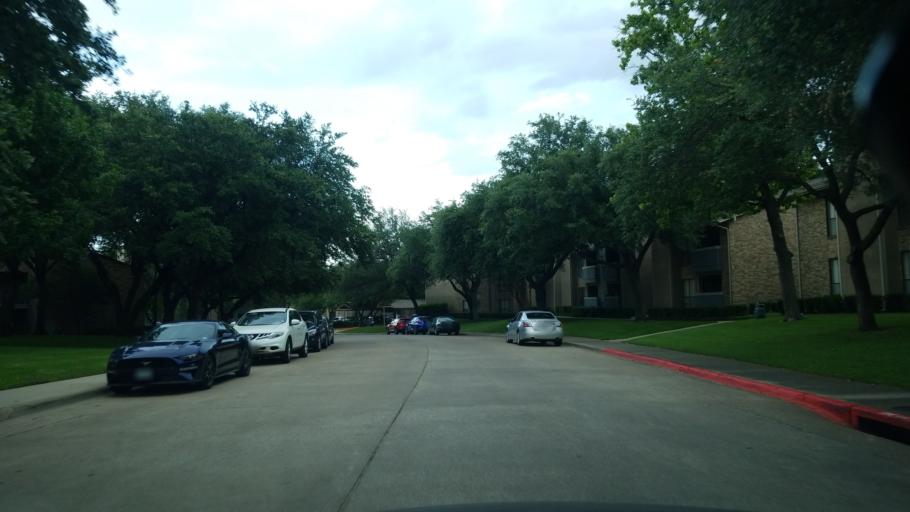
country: US
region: Texas
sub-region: Dallas County
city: Highland Park
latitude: 32.8540
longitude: -96.7666
